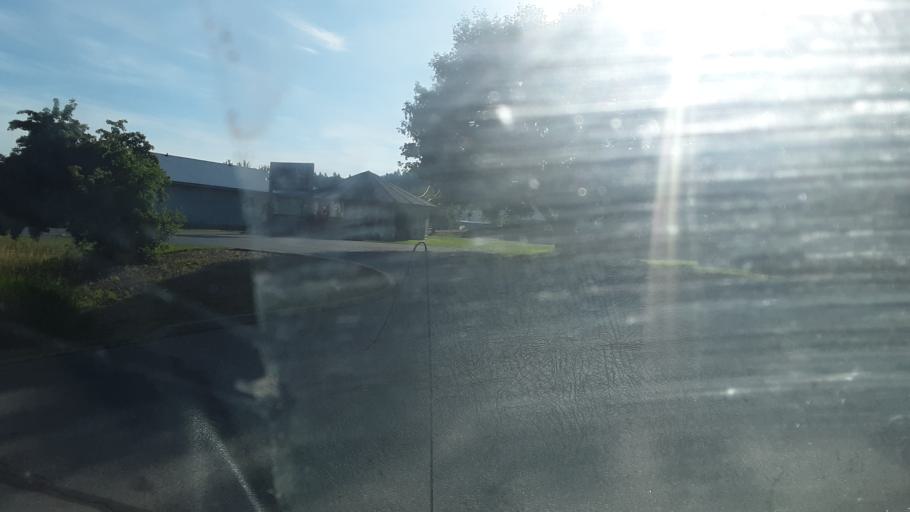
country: US
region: Idaho
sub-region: Boundary County
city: Bonners Ferry
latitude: 48.6787
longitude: -116.3286
